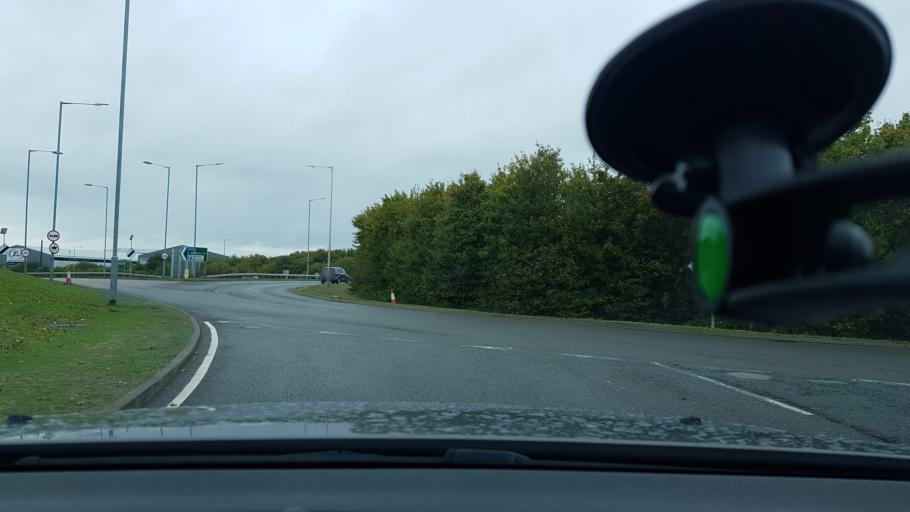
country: GB
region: England
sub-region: Essex
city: Takeley
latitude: 51.8771
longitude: 0.2480
